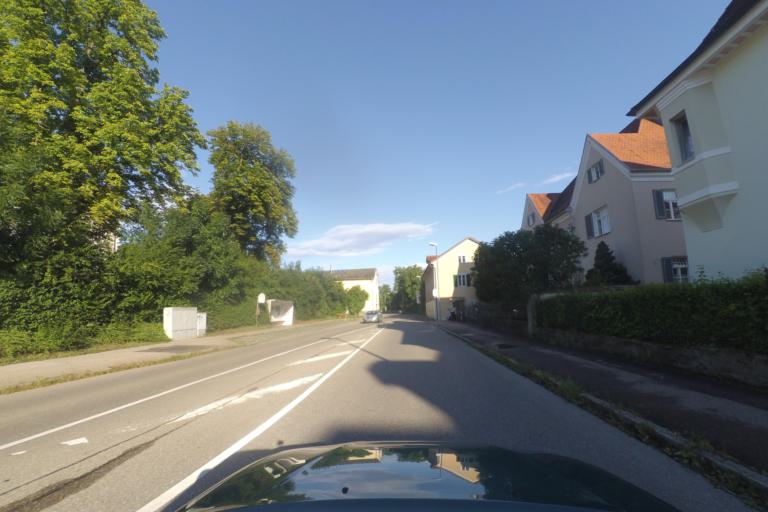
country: DE
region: Bavaria
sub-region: Upper Bavaria
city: Eichstaett
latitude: 48.8888
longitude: 11.1929
